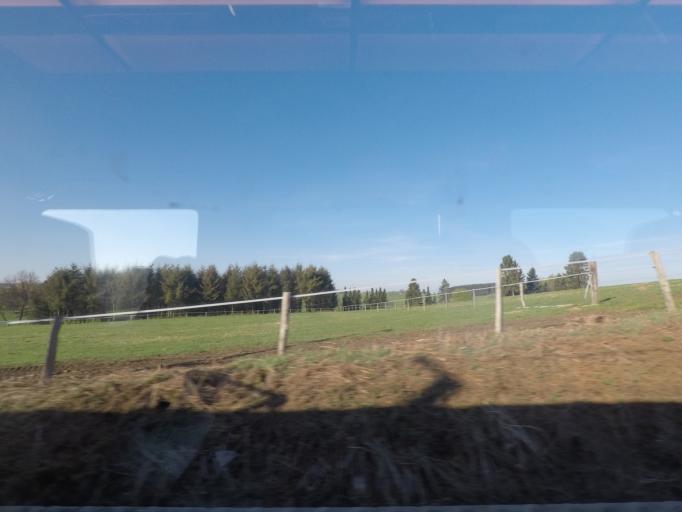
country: BE
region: Wallonia
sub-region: Province du Luxembourg
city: Neufchateau
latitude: 49.8149
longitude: 5.4796
